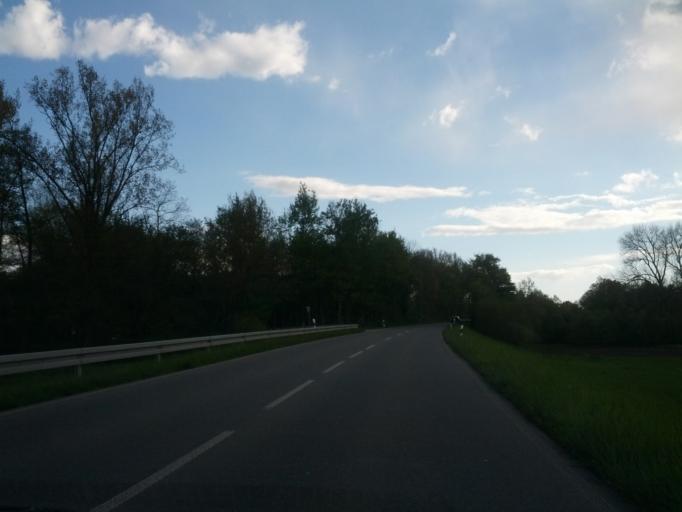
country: DE
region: Baden-Wuerttemberg
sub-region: Freiburg Region
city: Vorstetten
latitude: 48.0754
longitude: 7.8114
